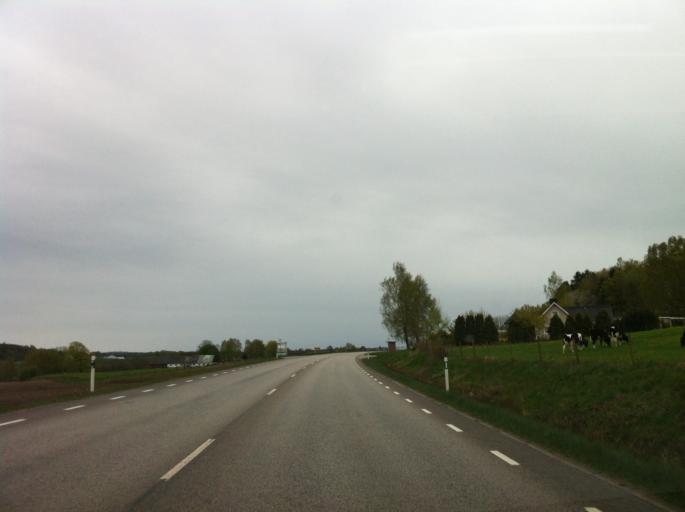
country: SE
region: Halland
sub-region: Falkenbergs Kommun
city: Falkenberg
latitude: 56.9752
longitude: 12.5765
